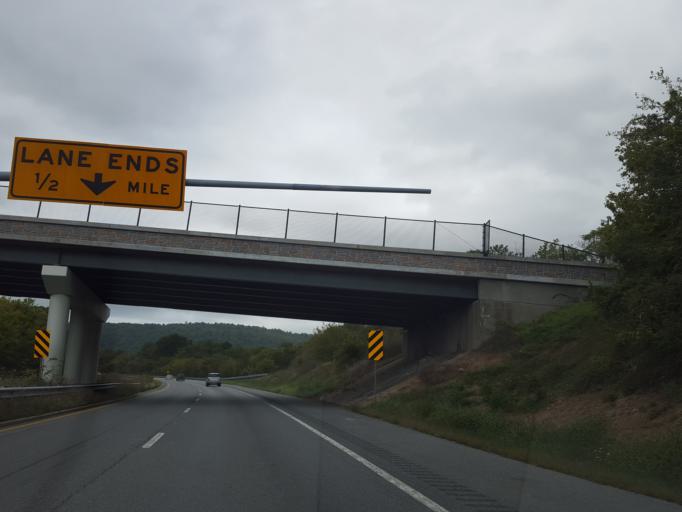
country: US
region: Maryland
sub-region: Frederick County
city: Brunswick
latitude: 39.3326
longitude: -77.6880
